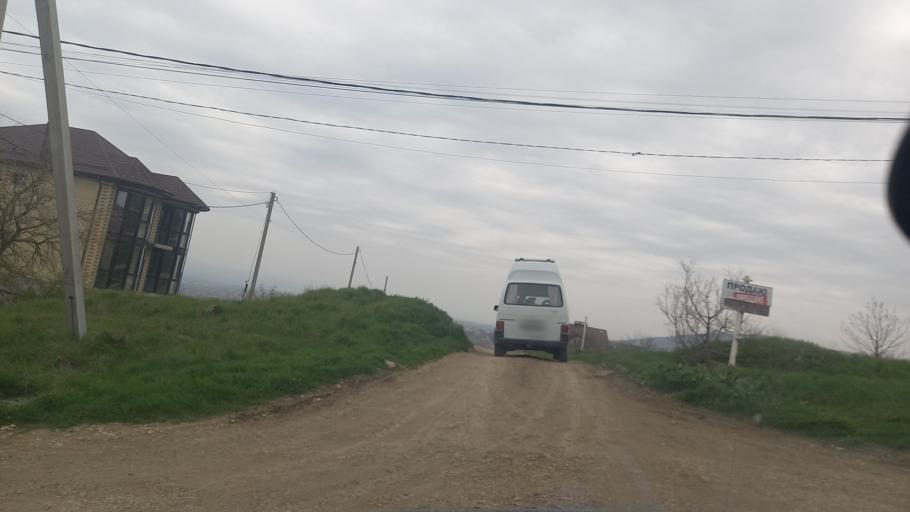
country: RU
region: Krasnodarskiy
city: Anapa
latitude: 44.8568
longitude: 37.3427
